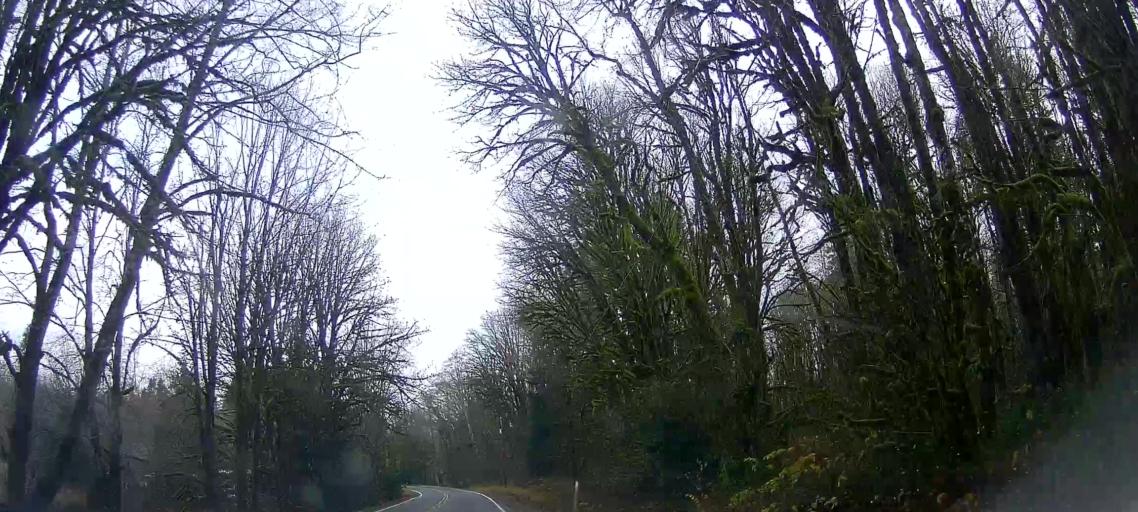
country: US
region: Washington
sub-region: Snohomish County
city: Darrington
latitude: 48.5197
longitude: -121.8427
